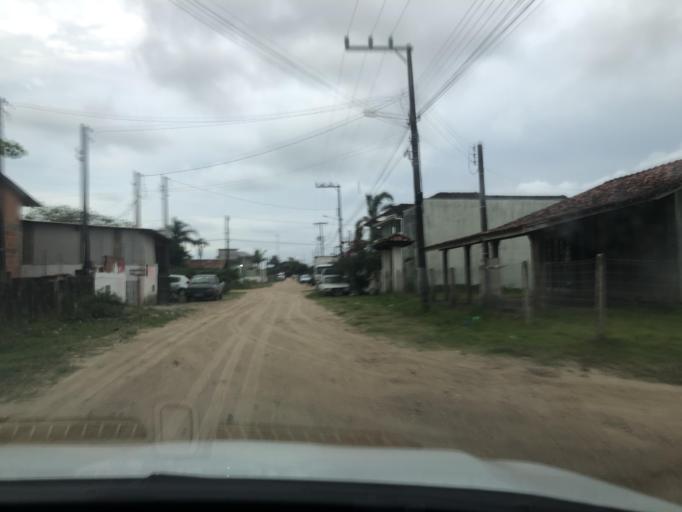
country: BR
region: Santa Catarina
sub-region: Sao Francisco Do Sul
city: Sao Francisco do Sul
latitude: -26.2353
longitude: -48.5208
